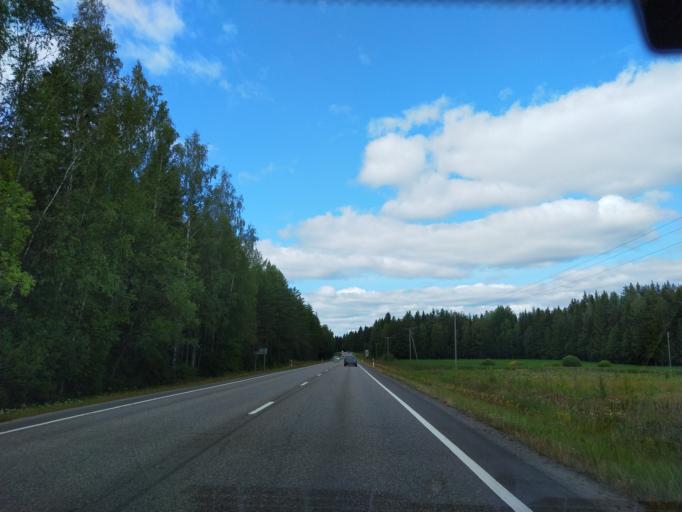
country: FI
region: Haeme
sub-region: Haemeenlinna
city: Renko
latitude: 60.7559
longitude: 24.3001
